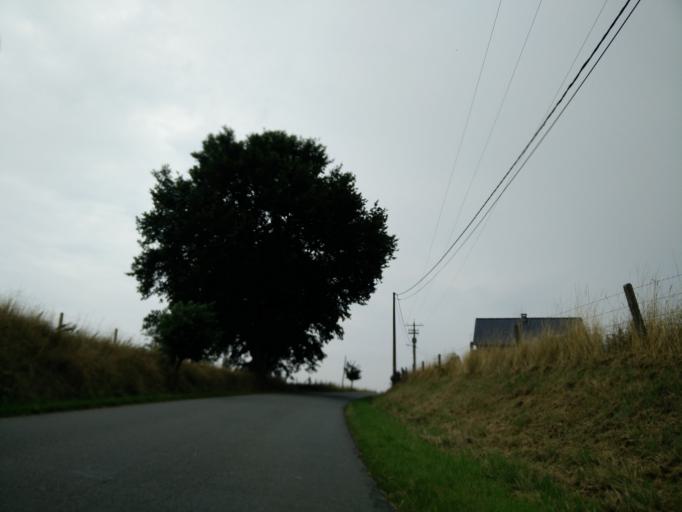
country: BE
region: Wallonia
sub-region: Province de Liege
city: Dalhem
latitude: 50.7174
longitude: 5.7550
